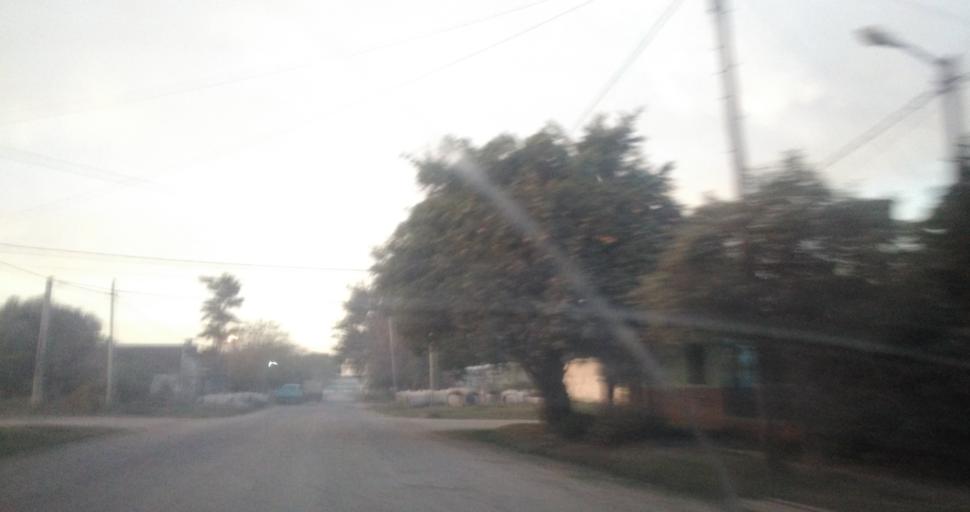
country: AR
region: Chaco
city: Fontana
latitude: -27.4364
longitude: -59.0216
